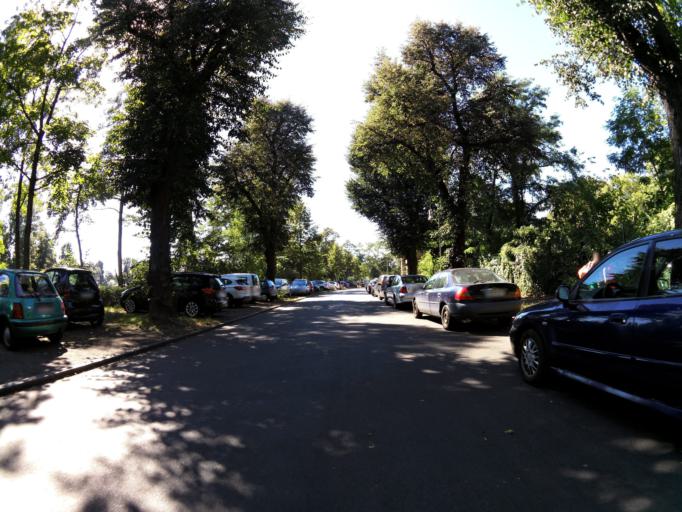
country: DE
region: Berlin
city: Moabit
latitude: 52.5412
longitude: 13.3299
